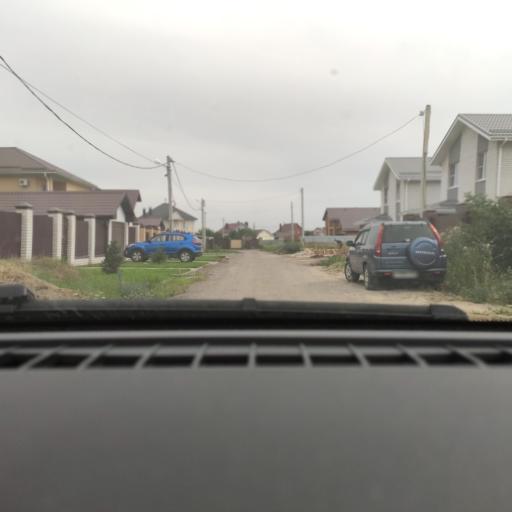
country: RU
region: Voronezj
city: Novaya Usman'
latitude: 51.6474
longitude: 39.3396
